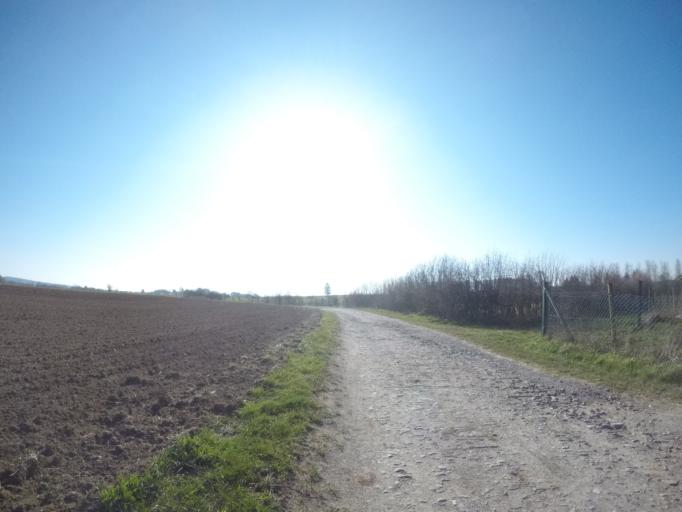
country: BE
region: Wallonia
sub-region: Province du Luxembourg
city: Habay-la-Vieille
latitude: 49.7147
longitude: 5.5707
